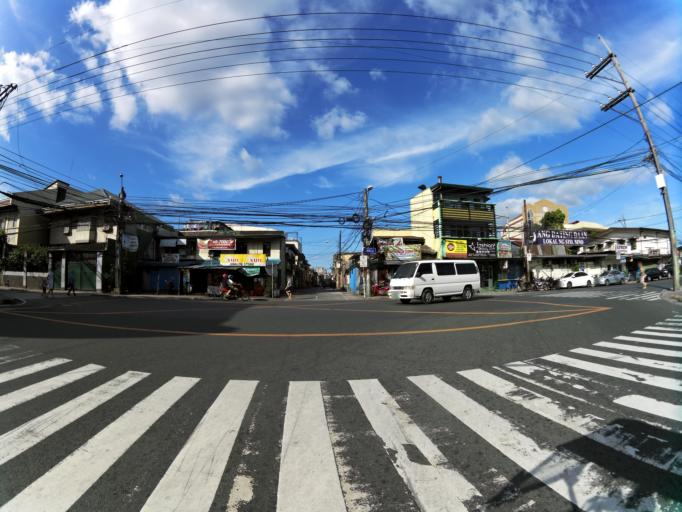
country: PH
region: Metro Manila
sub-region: Marikina
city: Calumpang
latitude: 14.6377
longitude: 121.0974
